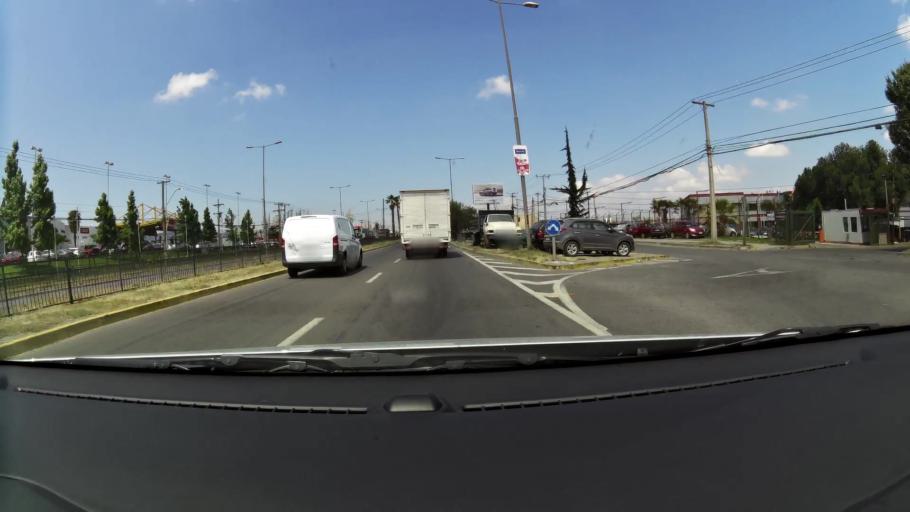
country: CL
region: Santiago Metropolitan
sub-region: Provincia de Santiago
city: Lo Prado
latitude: -33.5163
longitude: -70.7204
